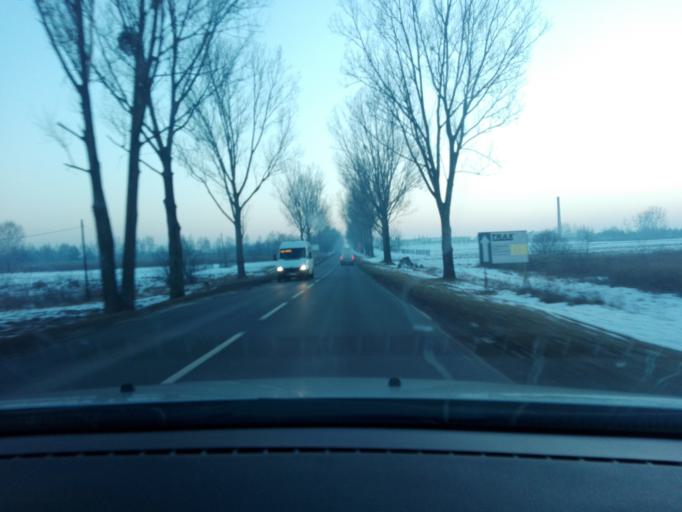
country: PL
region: Lodz Voivodeship
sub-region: Powiat zgierski
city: Zgierz
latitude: 51.9008
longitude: 19.4261
